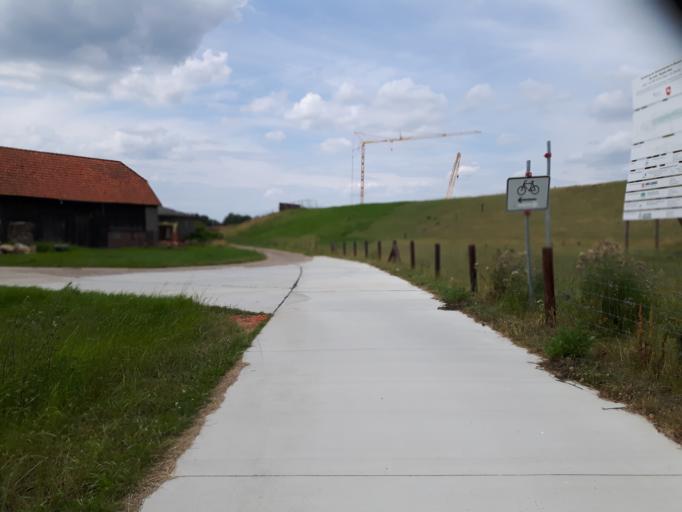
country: DE
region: Lower Saxony
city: Varel
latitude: 53.3905
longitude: 8.2115
